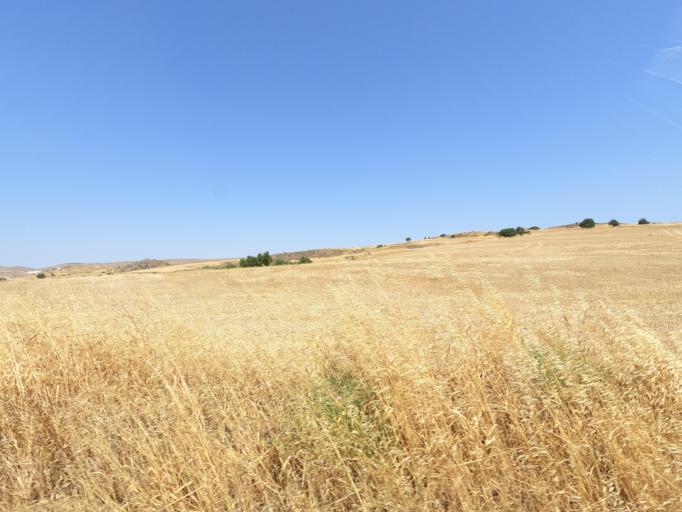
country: CY
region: Larnaka
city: Troulloi
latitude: 35.0357
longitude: 33.6233
